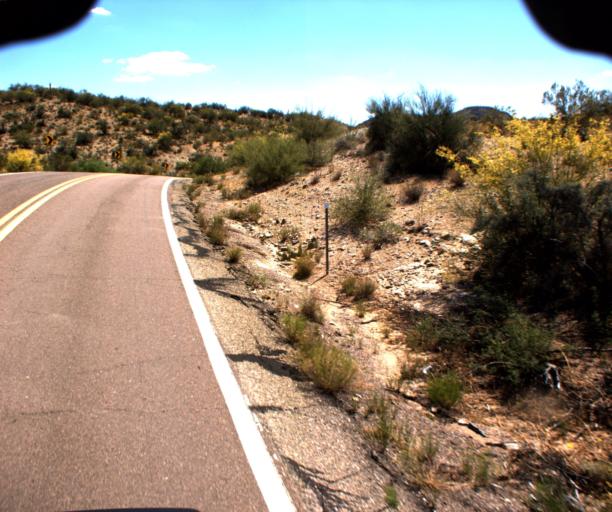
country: US
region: Arizona
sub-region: Yavapai County
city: Bagdad
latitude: 34.4368
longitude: -113.2403
